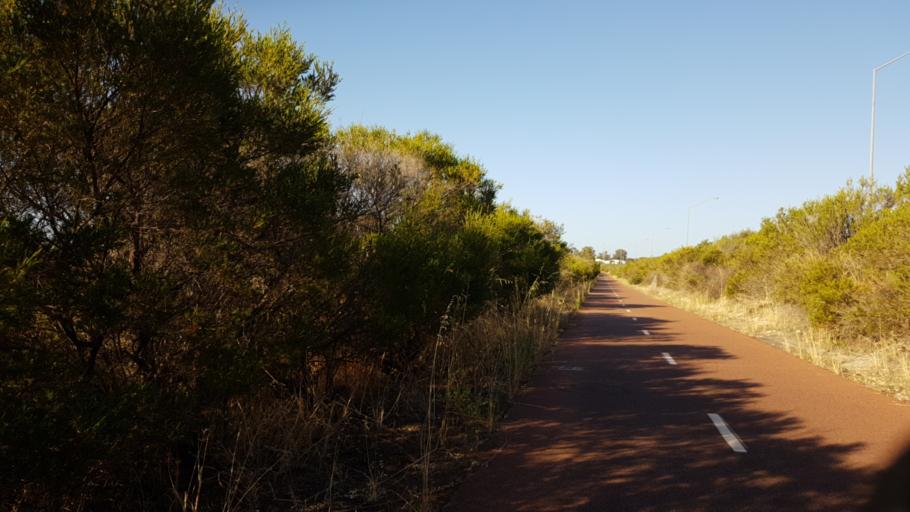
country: AU
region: Western Australia
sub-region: Kwinana
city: Wellard
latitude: -32.2676
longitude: 115.8483
